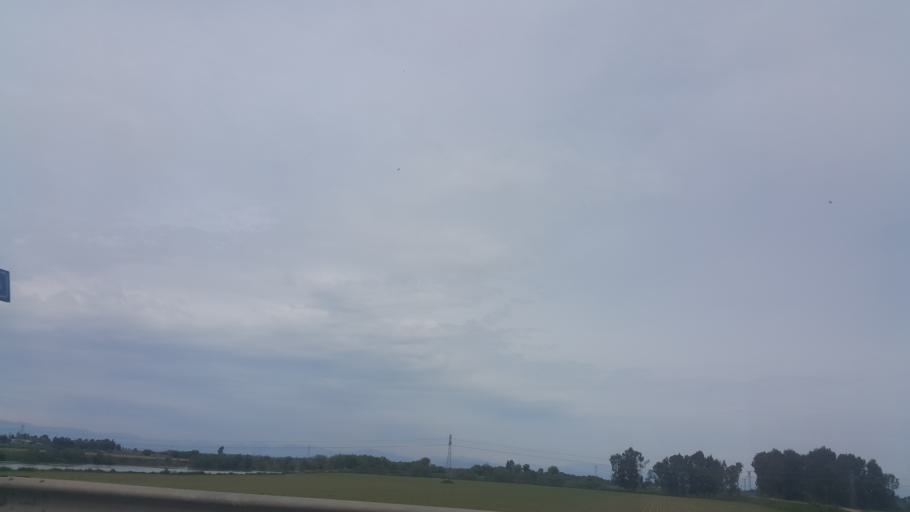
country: TR
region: Adana
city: Ceyhan
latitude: 37.0525
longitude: 35.8039
